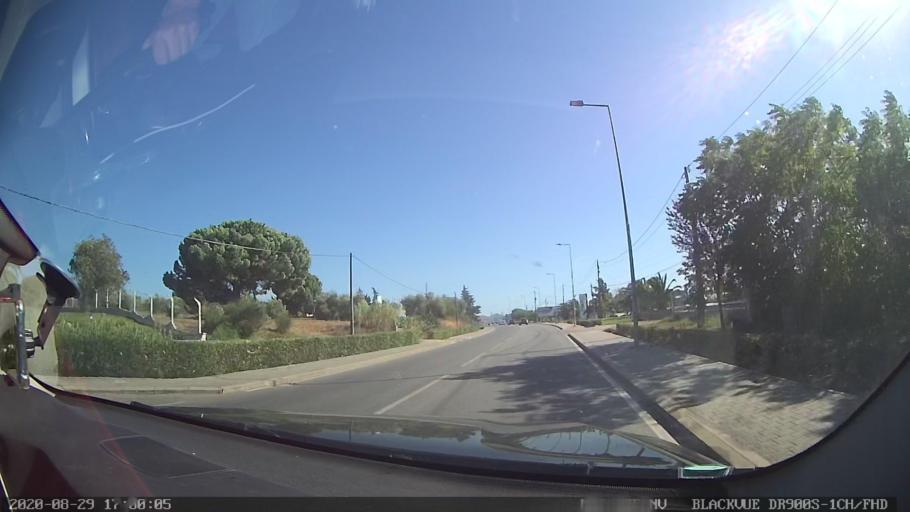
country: PT
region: Setubal
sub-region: Alcacer do Sal
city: Alcacer do Sal
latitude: 38.3820
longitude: -8.5135
